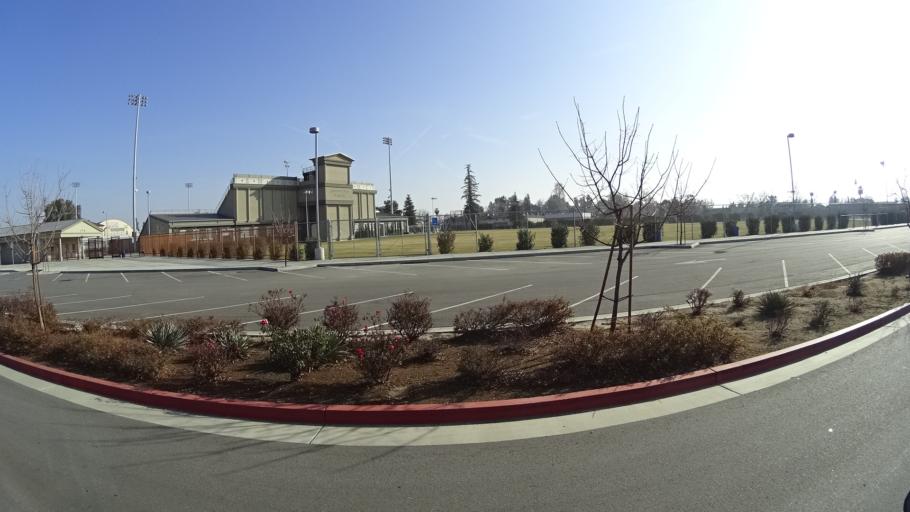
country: US
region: California
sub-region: Kern County
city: Bakersfield
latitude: 35.3702
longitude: -119.0279
